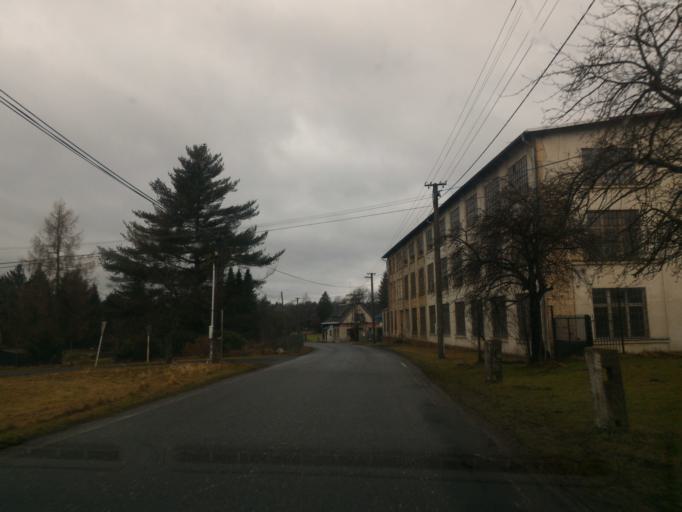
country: CZ
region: Ustecky
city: Stare Krecany
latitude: 50.9321
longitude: 14.4755
